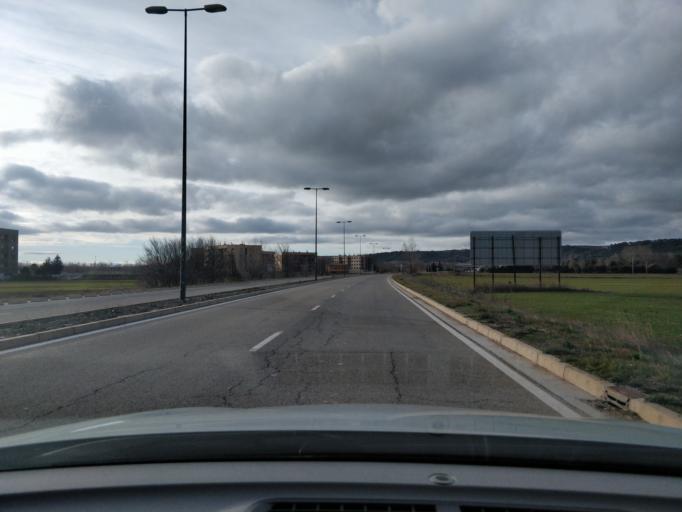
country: ES
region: Castille and Leon
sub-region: Provincia de Burgos
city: Villalbilla de Burgos
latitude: 42.3549
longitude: -3.7532
